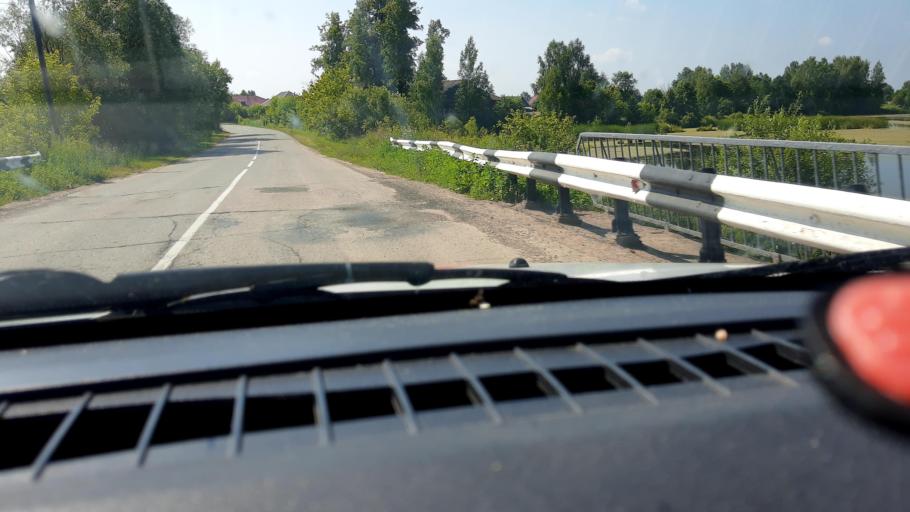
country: RU
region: Nizjnij Novgorod
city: Sharanga
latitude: 57.0536
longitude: 46.5451
